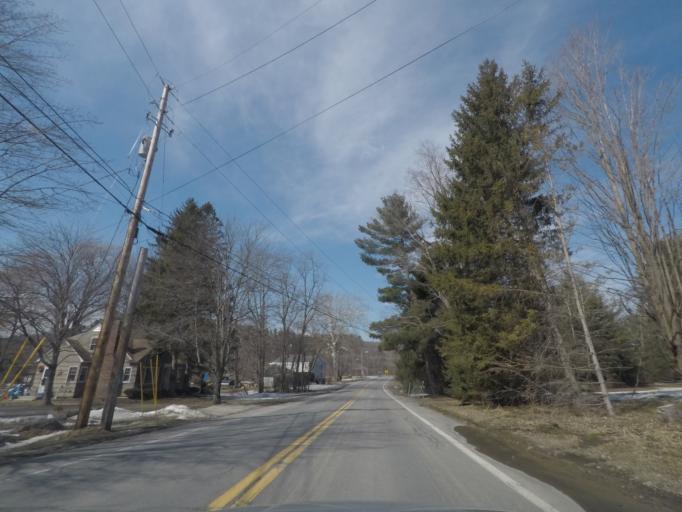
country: US
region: Massachusetts
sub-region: Berkshire County
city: Richmond
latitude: 42.4726
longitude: -73.3806
